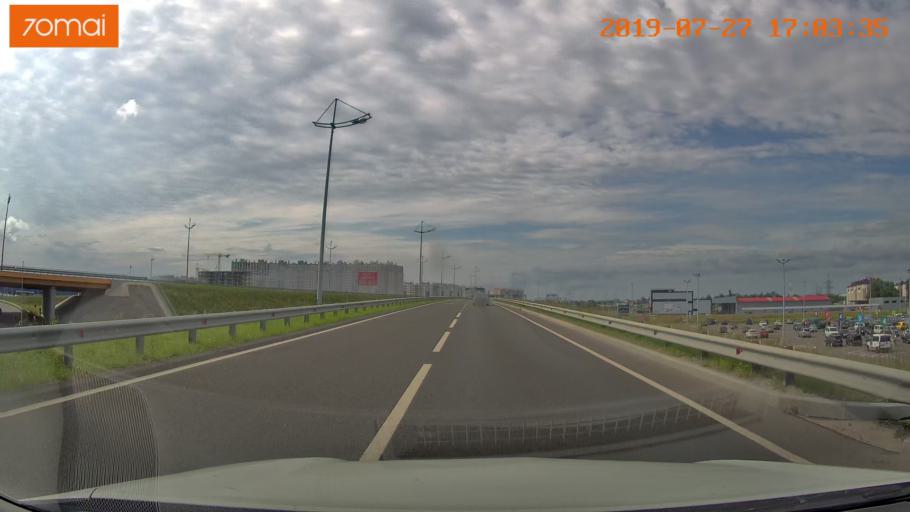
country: RU
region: Kaliningrad
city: Bol'shoe Isakovo
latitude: 54.7060
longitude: 20.6004
